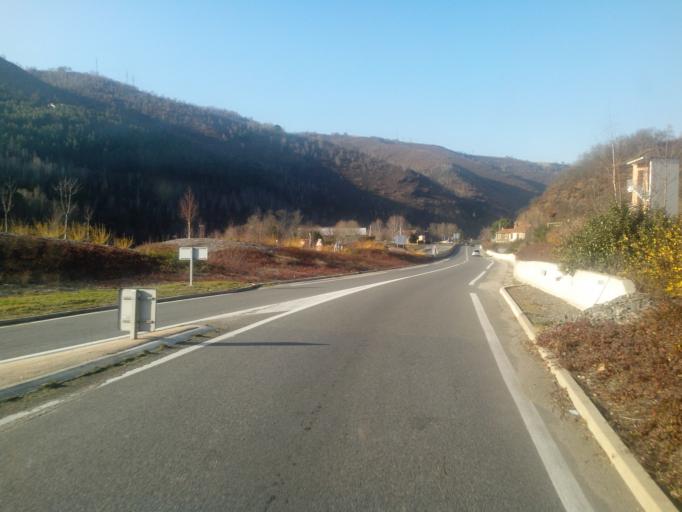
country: FR
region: Midi-Pyrenees
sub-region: Departement de l'Aveyron
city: Viviez
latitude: 44.5594
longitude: 2.2195
